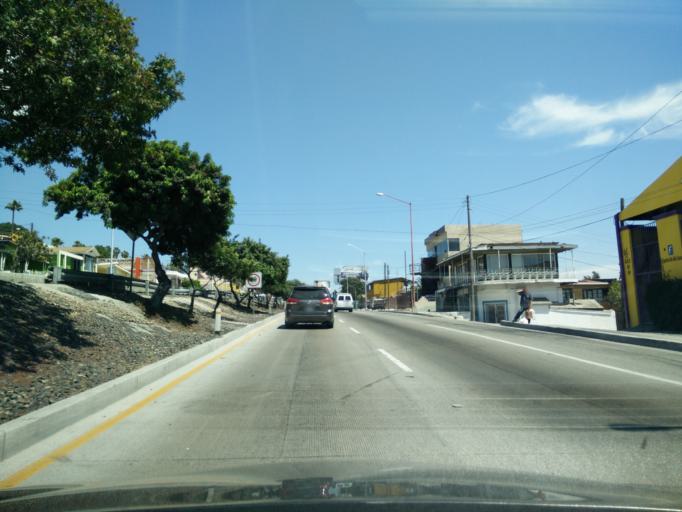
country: MX
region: Baja California
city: Tijuana
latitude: 32.5348
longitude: -117.0065
